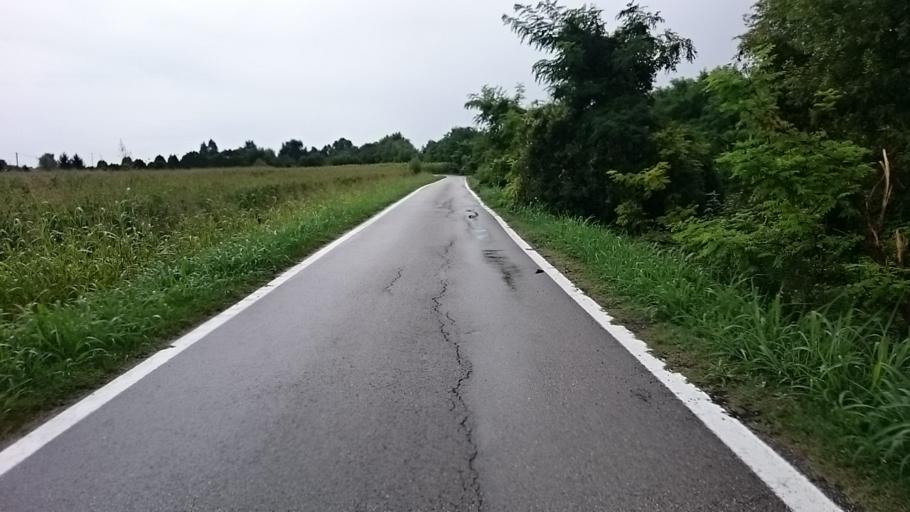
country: IT
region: Veneto
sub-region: Provincia di Treviso
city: Villa d'Asolo
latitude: 45.7583
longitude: 11.8799
